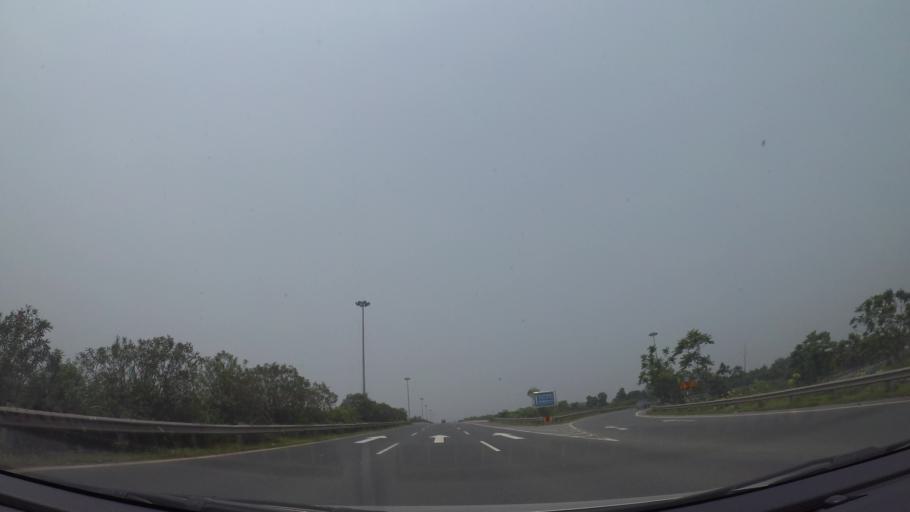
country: VN
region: Ha Noi
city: Lien Quan
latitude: 20.9904
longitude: 105.5285
